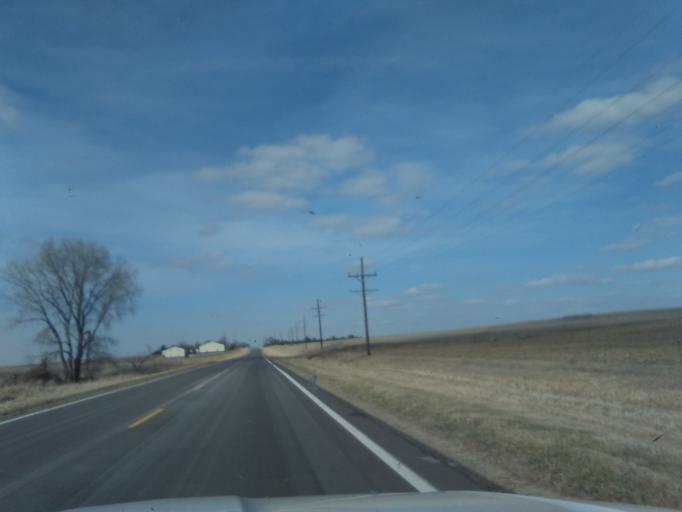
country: US
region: Nebraska
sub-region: Gage County
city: Beatrice
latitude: 40.1238
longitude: -96.9355
